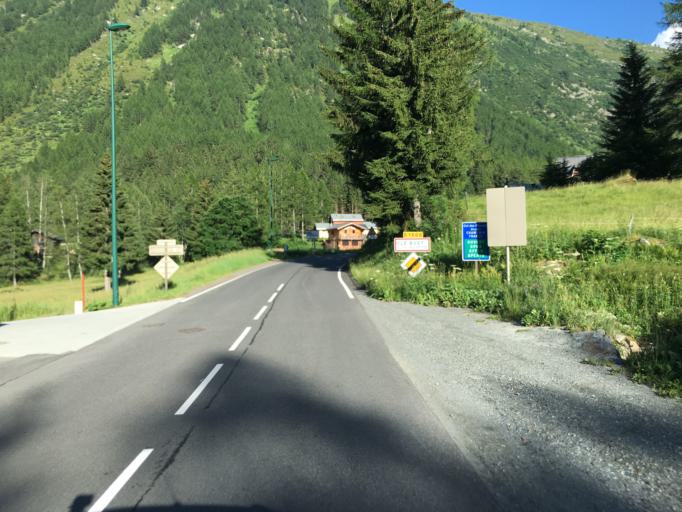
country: FR
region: Rhone-Alpes
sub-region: Departement de la Haute-Savoie
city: Chamonix-Mont-Blanc
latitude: 46.0204
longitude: 6.9185
